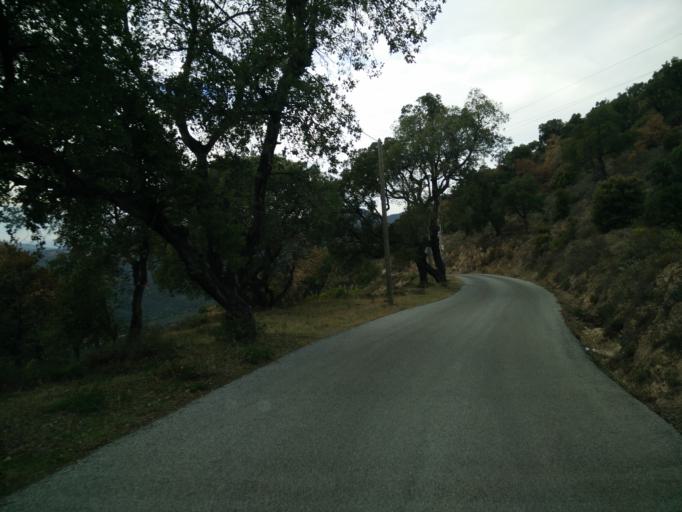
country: FR
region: Provence-Alpes-Cote d'Azur
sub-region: Departement du Var
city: Sainte-Maxime
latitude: 43.3632
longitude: 6.6095
